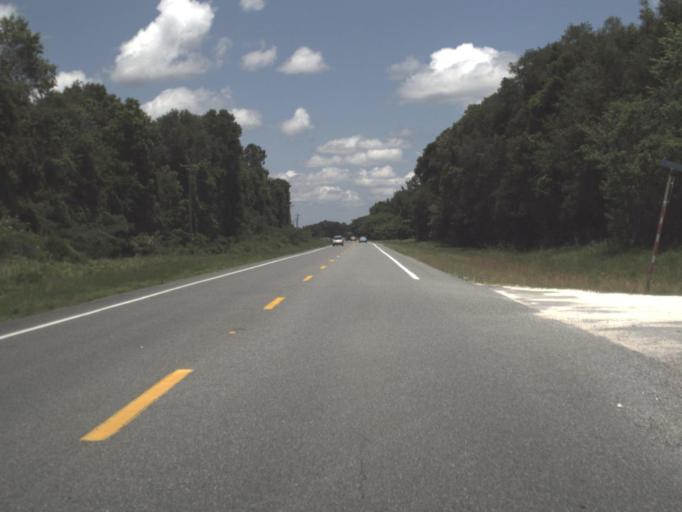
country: US
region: Florida
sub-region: Alachua County
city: High Springs
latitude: 29.8927
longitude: -82.6770
